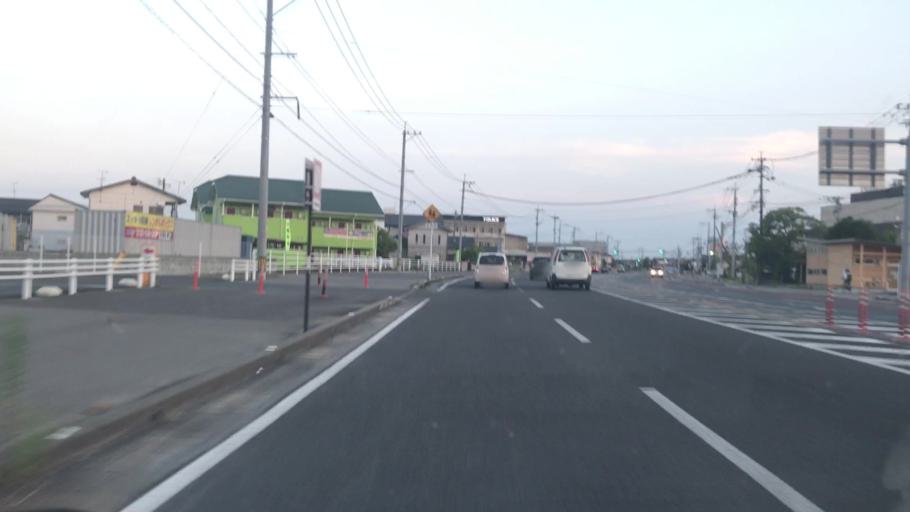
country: JP
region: Saga Prefecture
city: Saga-shi
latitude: 33.2388
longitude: 130.2945
